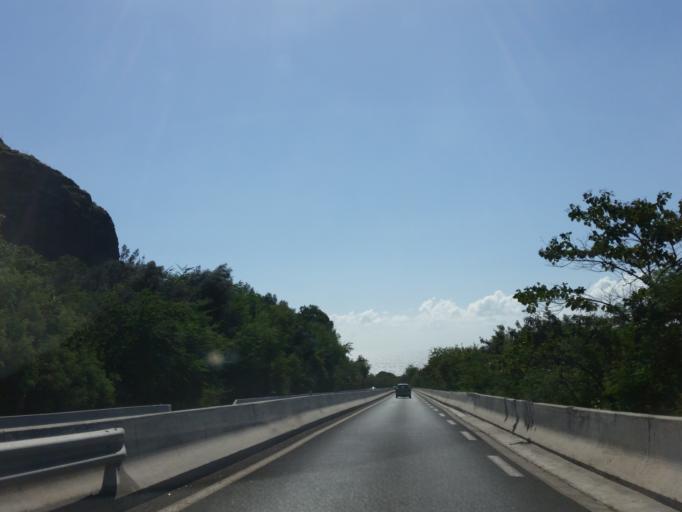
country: RE
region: Reunion
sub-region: Reunion
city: Saint-Denis
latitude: -20.8827
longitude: 55.4391
